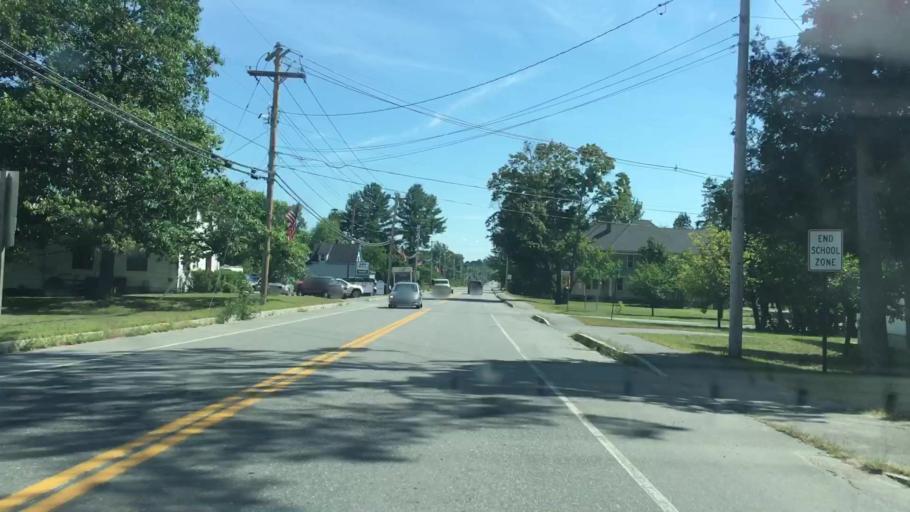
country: US
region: Maine
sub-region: Piscataquis County
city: Milo
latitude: 45.2492
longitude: -68.9806
